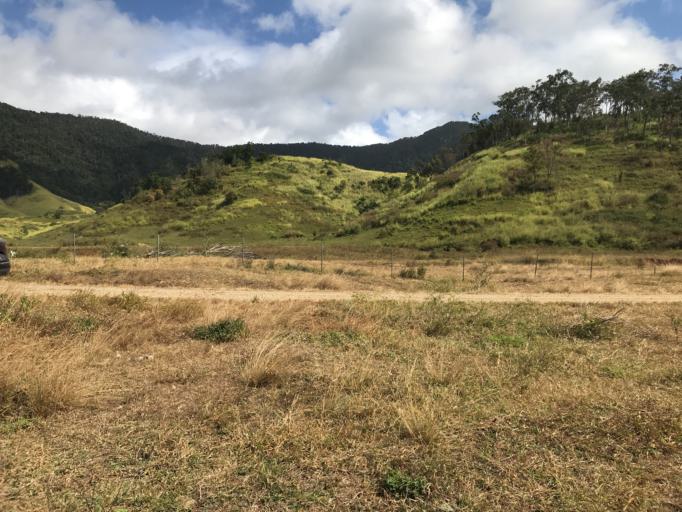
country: AU
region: Queensland
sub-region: Whitsunday
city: Proserpine
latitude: -20.8546
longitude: 148.6154
